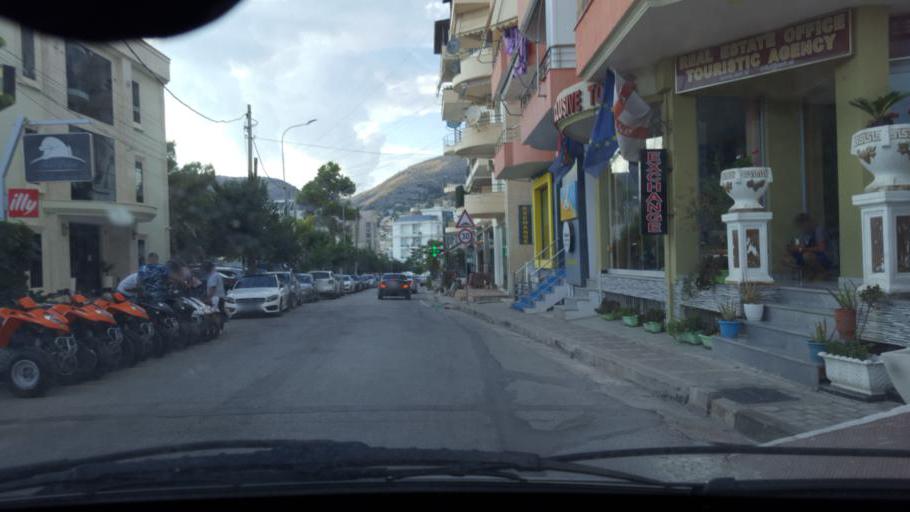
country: AL
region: Vlore
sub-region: Rrethi i Sarandes
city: Sarande
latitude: 39.8681
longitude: 20.0152
